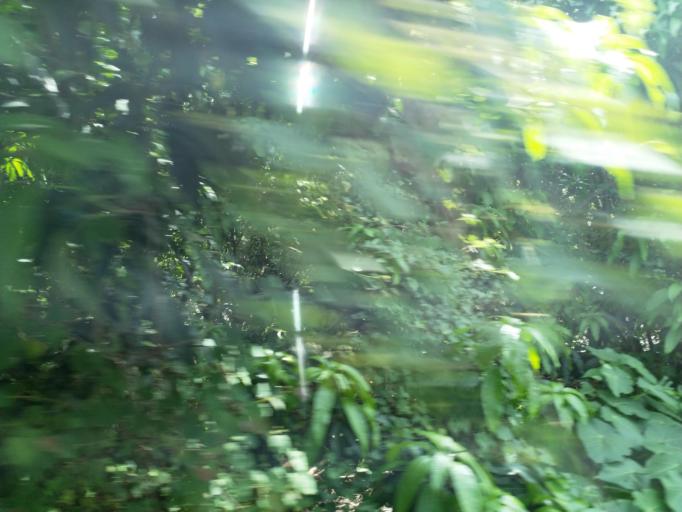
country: TW
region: Taiwan
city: Yujing
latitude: 22.9307
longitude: 120.5873
